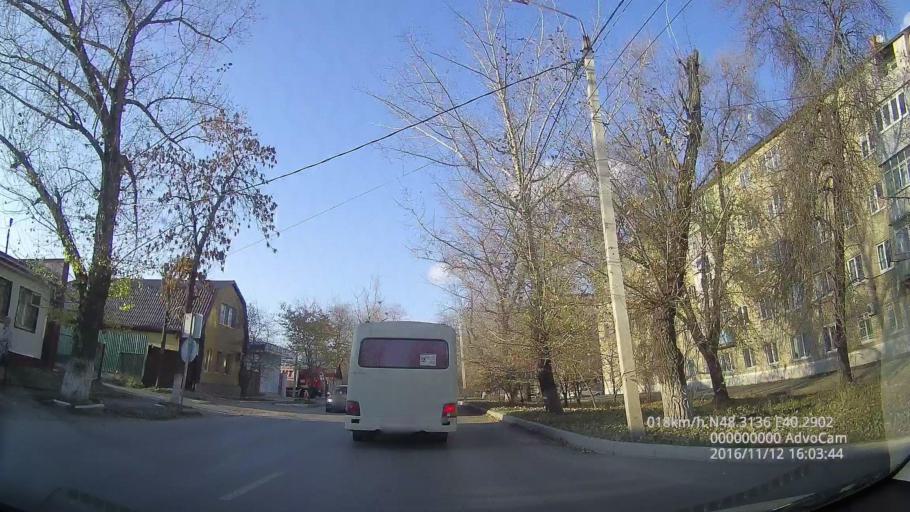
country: RU
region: Rostov
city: Staraya Stanitsa
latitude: 48.3137
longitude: 40.2901
